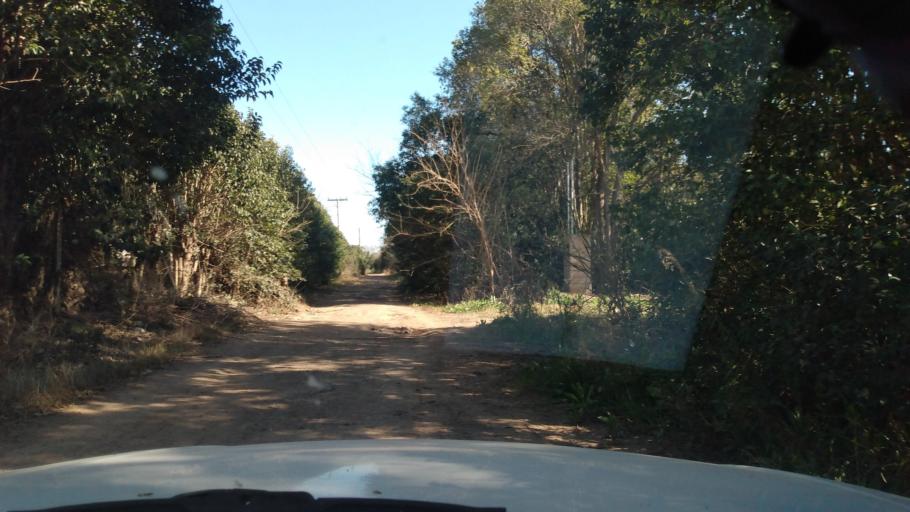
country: AR
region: Buenos Aires
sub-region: Partido de Mercedes
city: Mercedes
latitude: -34.6632
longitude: -59.3967
